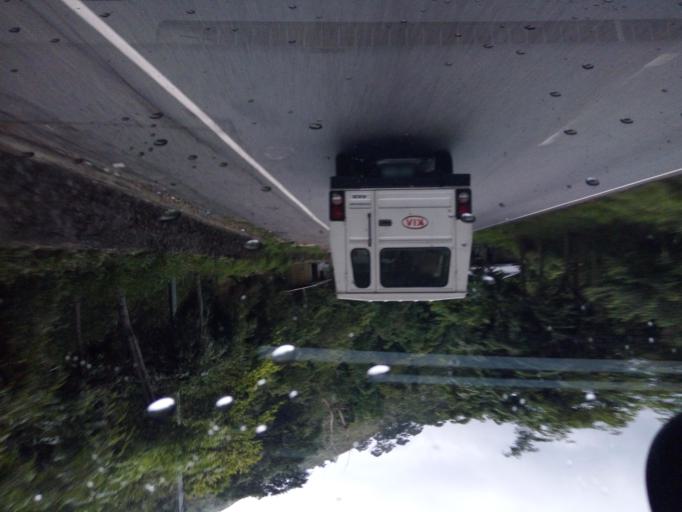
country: PH
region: Cagayan Valley
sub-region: Province of Nueva Vizcaya
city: Santa Fe
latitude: 16.1148
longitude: 120.9267
